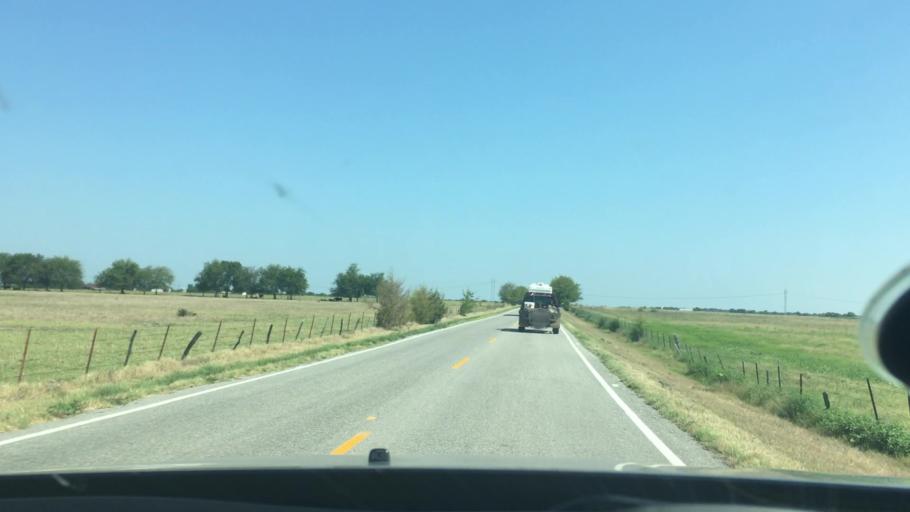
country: US
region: Oklahoma
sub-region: Johnston County
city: Tishomingo
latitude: 34.1556
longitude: -96.5066
